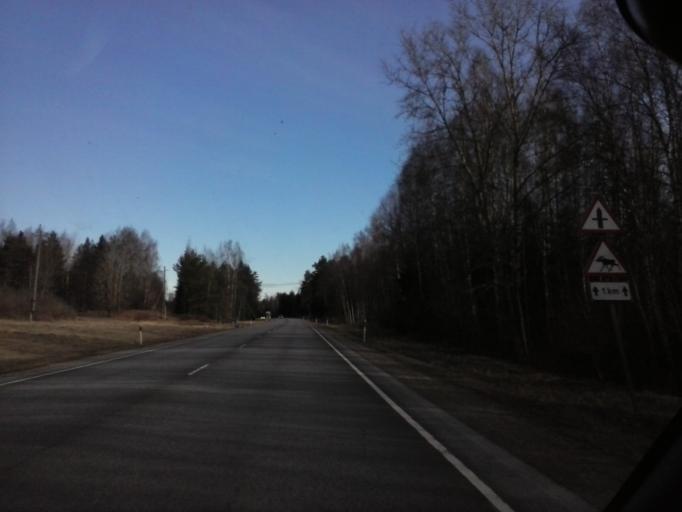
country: EE
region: Harju
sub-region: Anija vald
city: Kehra
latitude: 59.1239
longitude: 25.3178
